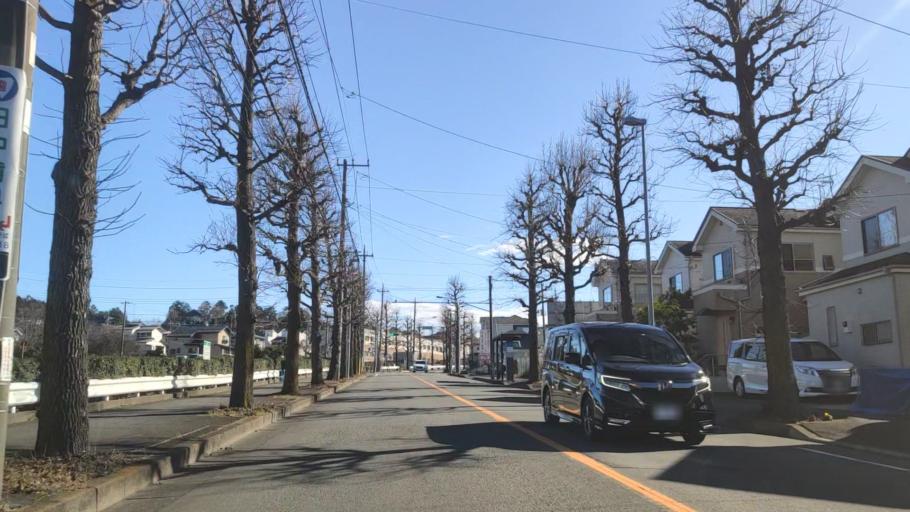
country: JP
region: Tokyo
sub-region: Machida-shi
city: Machida
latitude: 35.5196
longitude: 139.5073
